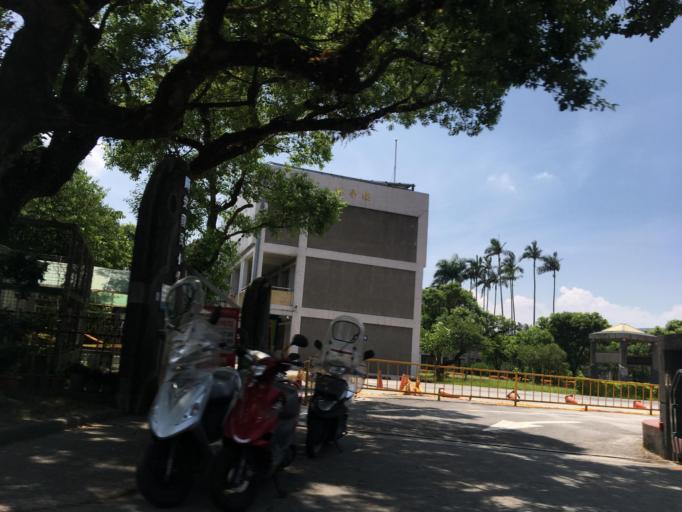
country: TW
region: Taiwan
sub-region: Yilan
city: Yilan
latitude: 24.6537
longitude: 121.7635
